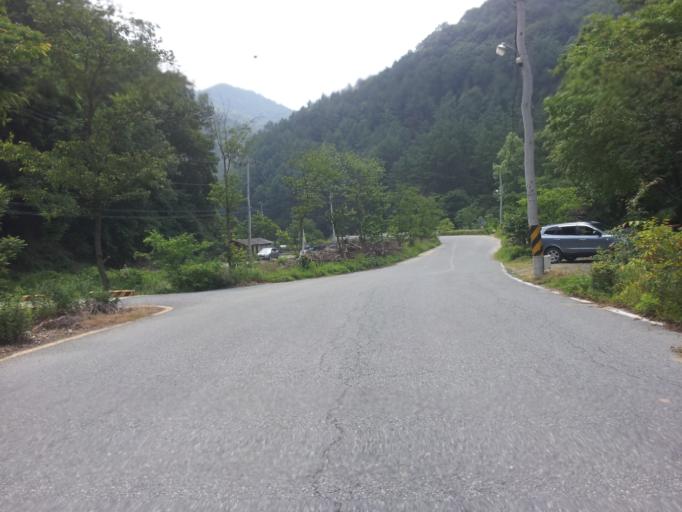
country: KR
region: Daejeon
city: Daejeon
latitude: 36.3326
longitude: 127.4906
